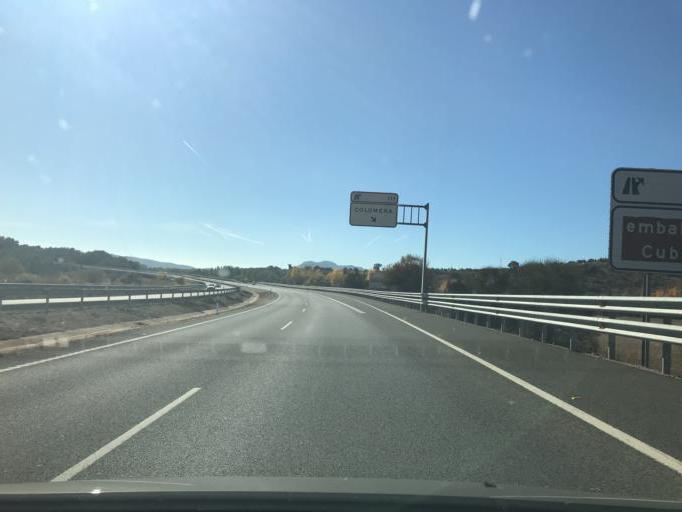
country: ES
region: Andalusia
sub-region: Provincia de Granada
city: Calicasas
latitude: 37.3064
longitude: -3.6565
